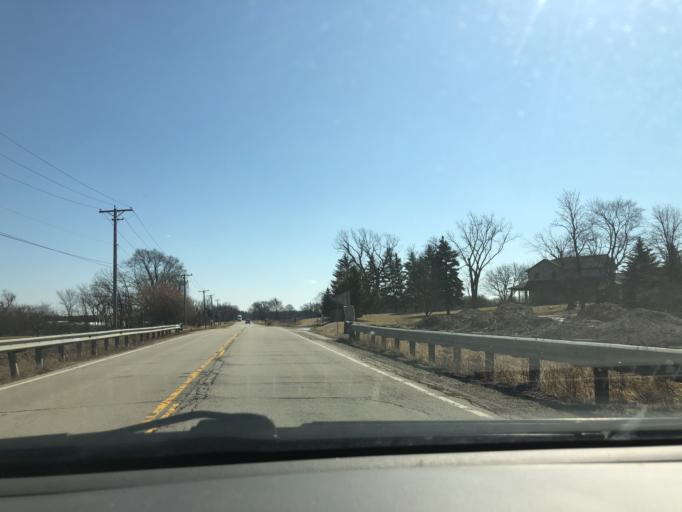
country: US
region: Illinois
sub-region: Kane County
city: Hampshire
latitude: 42.0967
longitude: -88.4775
